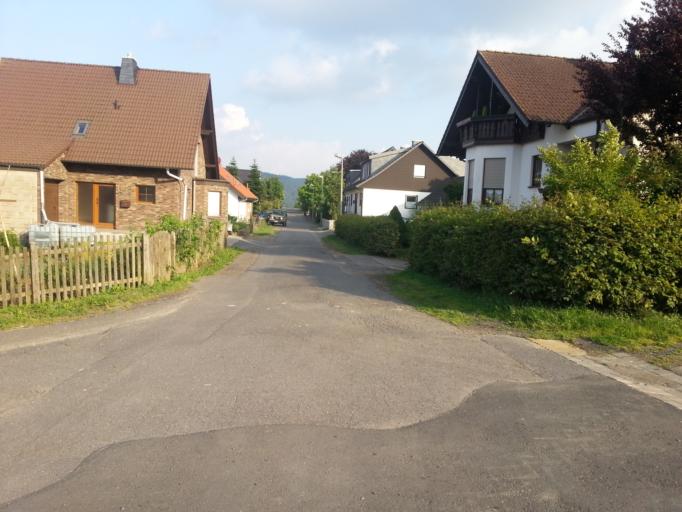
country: DE
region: Rheinland-Pfalz
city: Spessart
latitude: 50.4880
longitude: 7.0946
